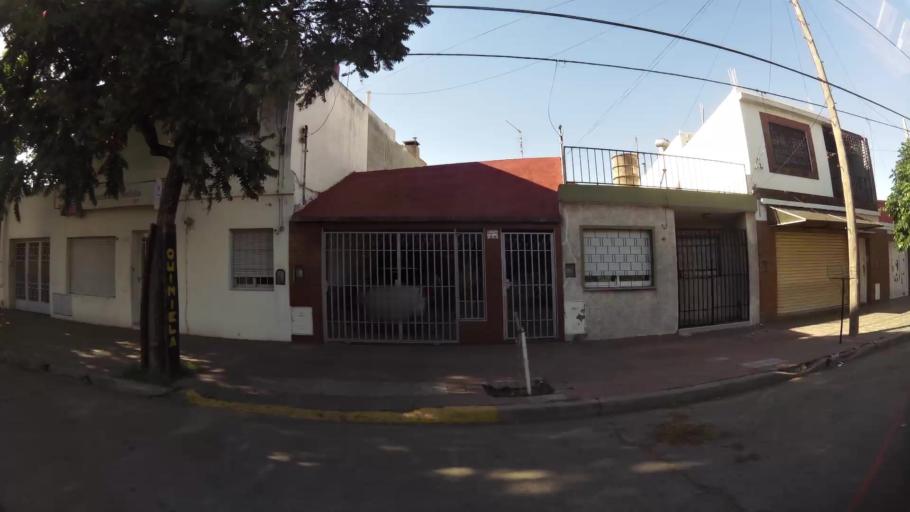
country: AR
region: Cordoba
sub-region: Departamento de Capital
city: Cordoba
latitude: -31.3897
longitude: -64.1751
